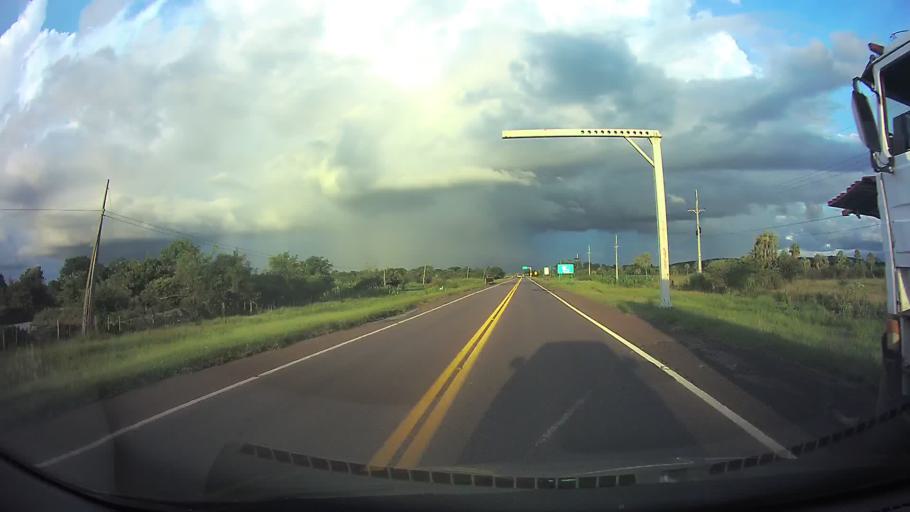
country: PY
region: Paraguari
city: Carapegua
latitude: -25.7520
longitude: -57.2231
